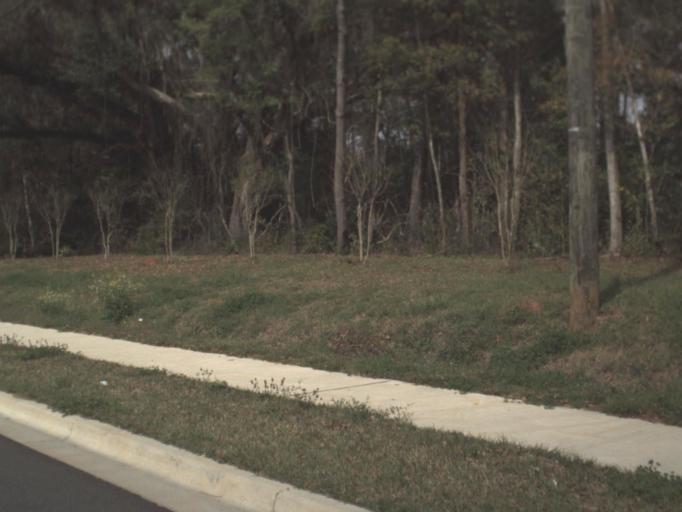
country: US
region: Florida
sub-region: Leon County
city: Tallahassee
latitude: 30.4793
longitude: -84.1749
